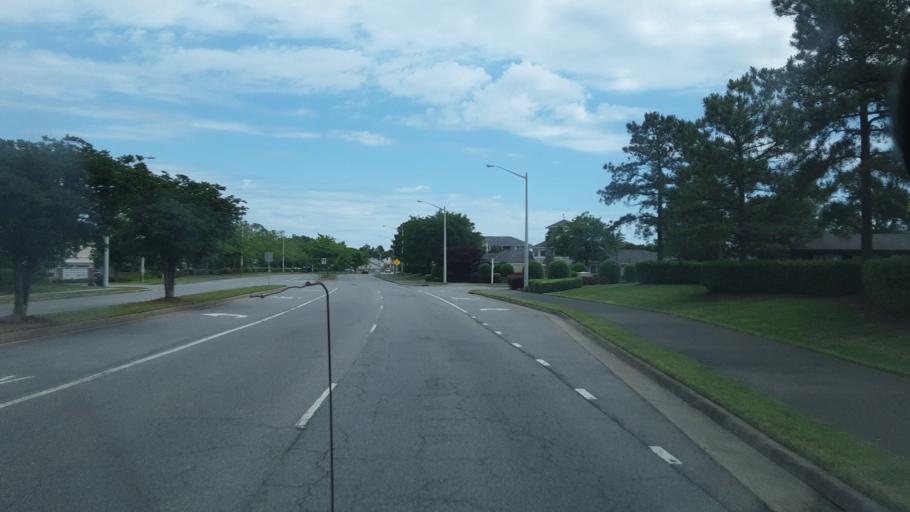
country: US
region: Virginia
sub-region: City of Virginia Beach
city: Virginia Beach
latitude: 36.7577
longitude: -76.0061
